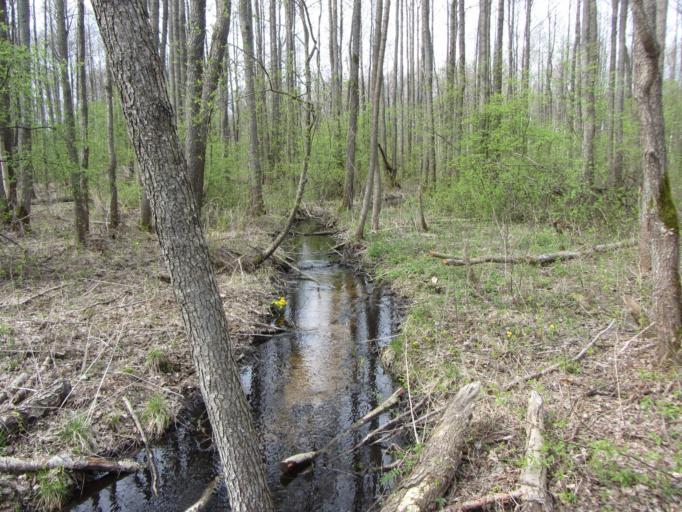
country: LT
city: Zarasai
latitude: 55.5785
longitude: 26.1513
